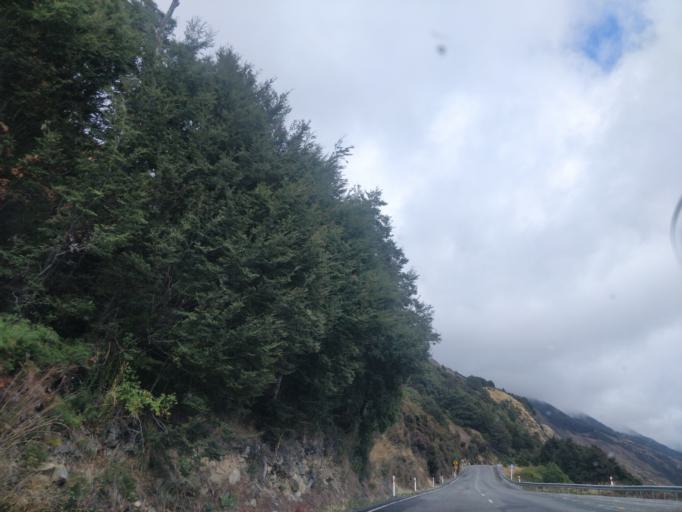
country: NZ
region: Canterbury
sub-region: Waimakariri District
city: Oxford
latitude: -43.0183
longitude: 171.7059
